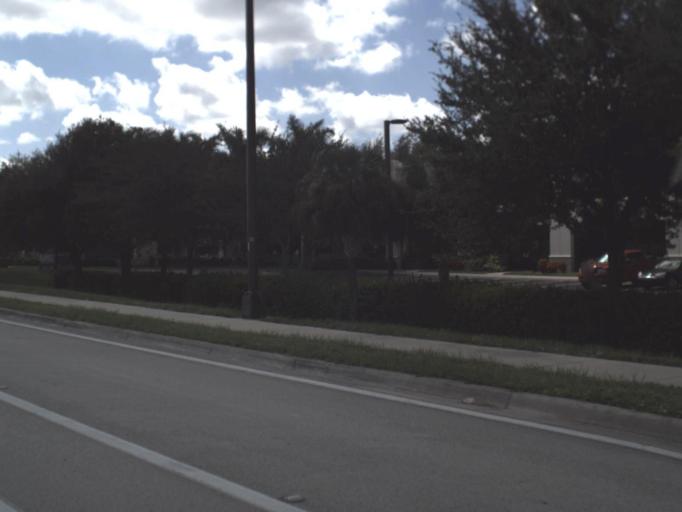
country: US
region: Florida
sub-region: Lee County
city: Bonita Springs
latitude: 26.3420
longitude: -81.8071
